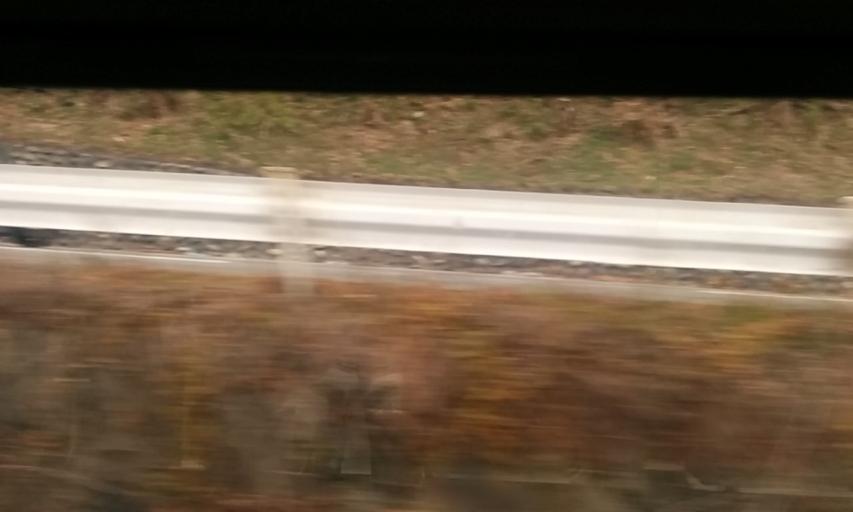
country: JP
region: Nagano
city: Matsumoto
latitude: 36.2431
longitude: 137.9538
